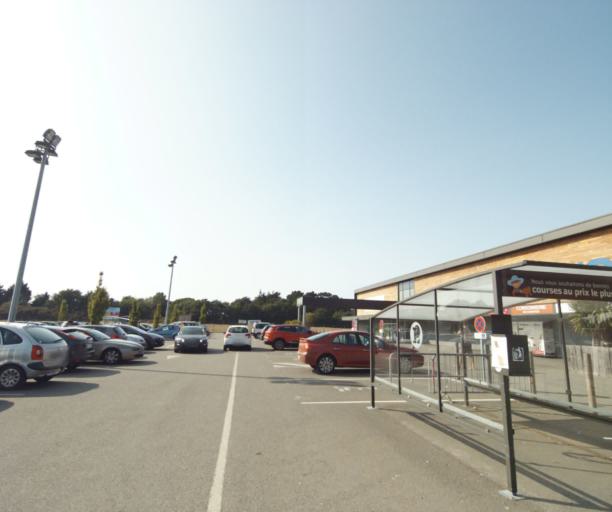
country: FR
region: Brittany
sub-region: Departement du Morbihan
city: Riantec
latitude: 47.7270
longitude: -3.3200
